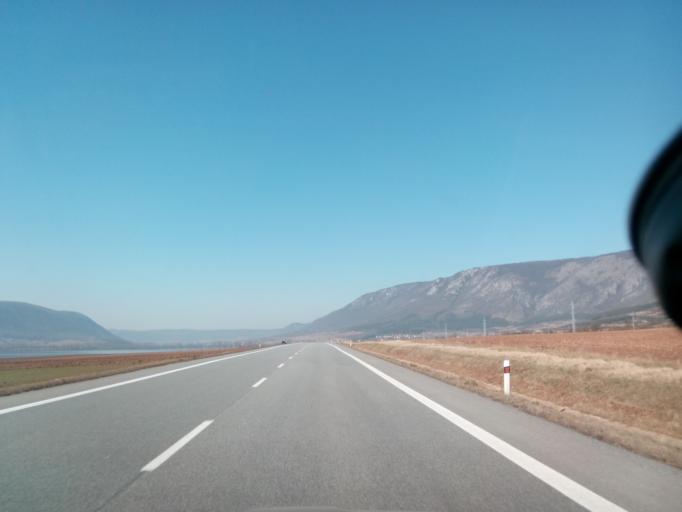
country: SK
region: Kosicky
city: Medzev
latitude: 48.6004
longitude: 20.7851
